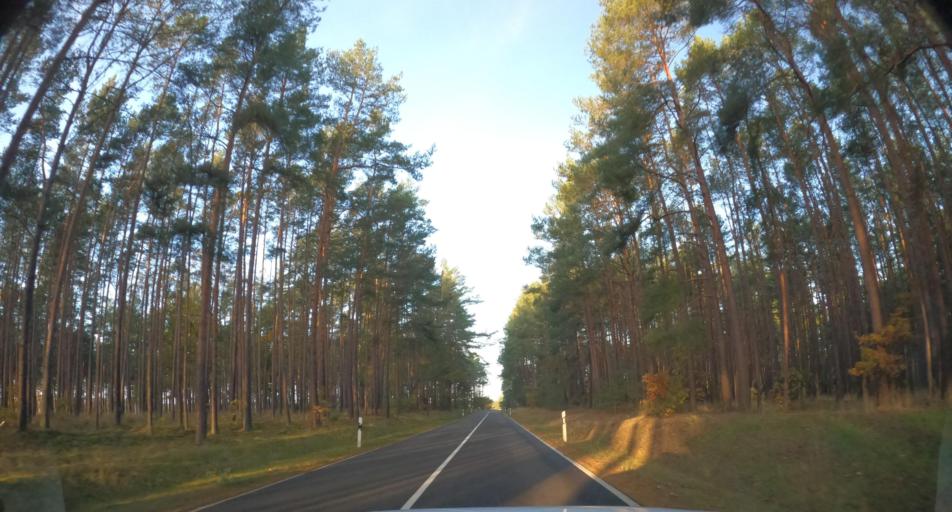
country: DE
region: Mecklenburg-Vorpommern
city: Ahlbeck
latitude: 53.6799
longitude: 14.1788
